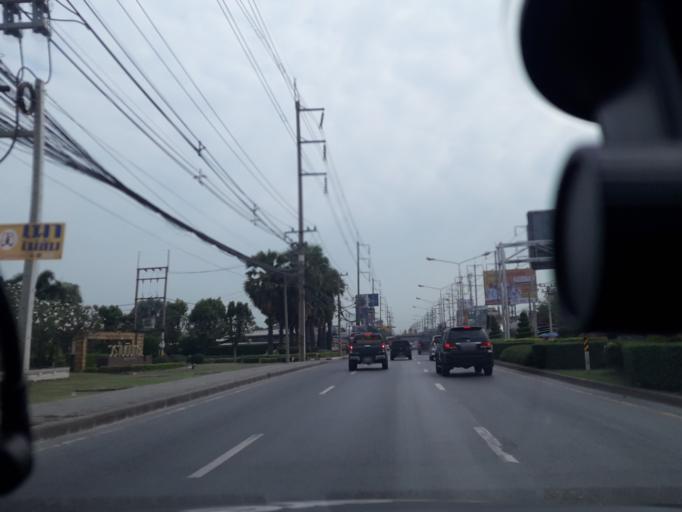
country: TH
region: Pathum Thani
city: Lam Luk Ka
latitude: 13.9340
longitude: 100.7155
